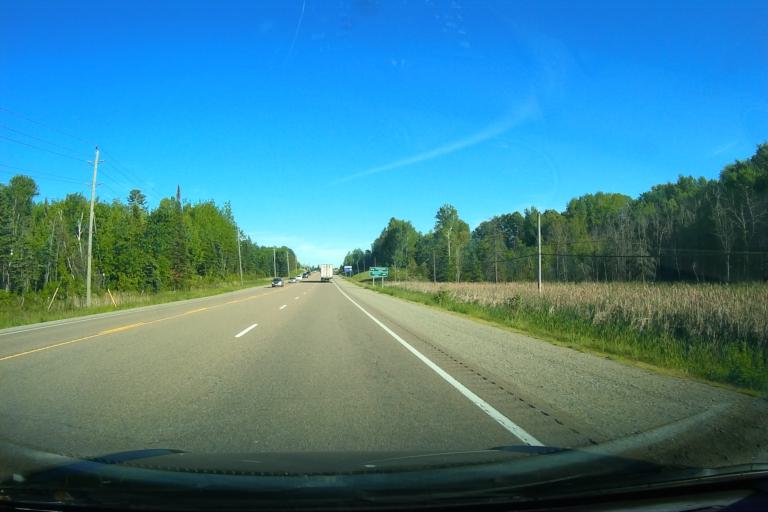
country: CA
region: Ontario
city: Renfrew
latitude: 45.6111
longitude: -76.8585
